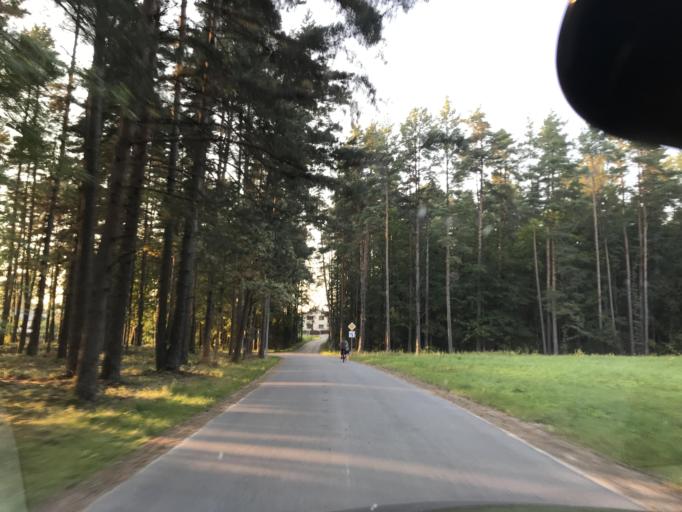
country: LV
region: Ikskile
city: Ikskile
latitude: 56.8256
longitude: 24.5087
